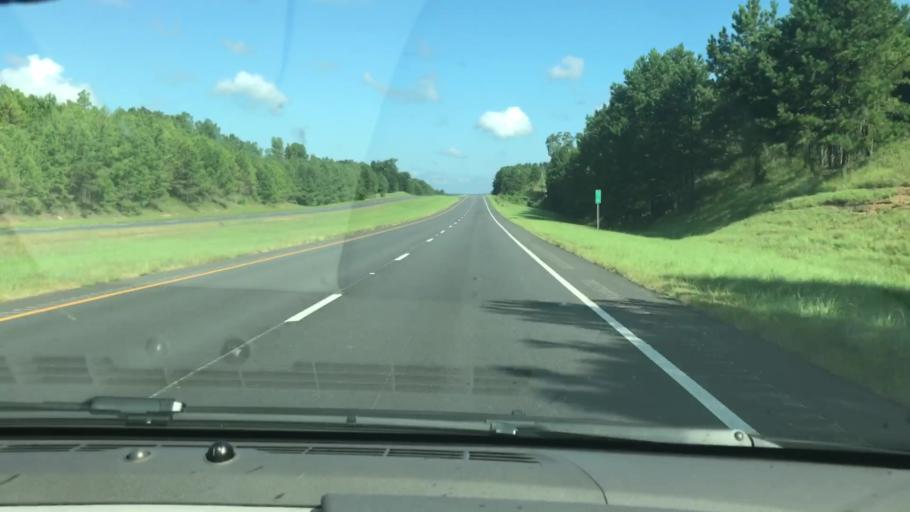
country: US
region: Alabama
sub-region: Barbour County
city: Eufaula
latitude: 32.0426
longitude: -85.1287
